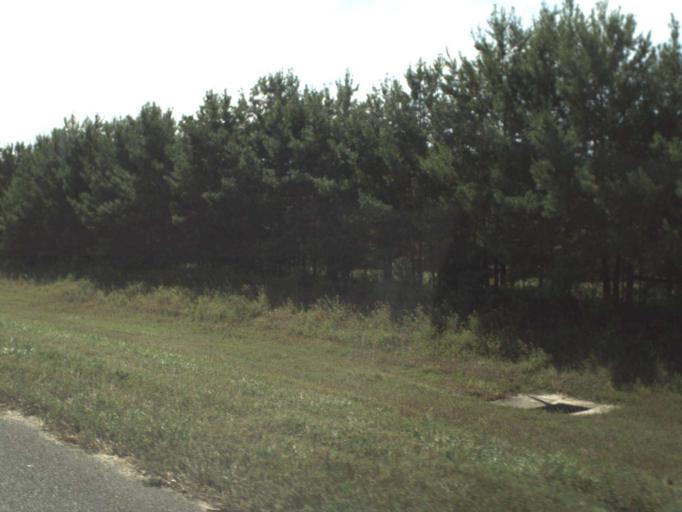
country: US
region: Florida
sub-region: Bay County
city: Lynn Haven
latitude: 30.4083
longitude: -85.6903
